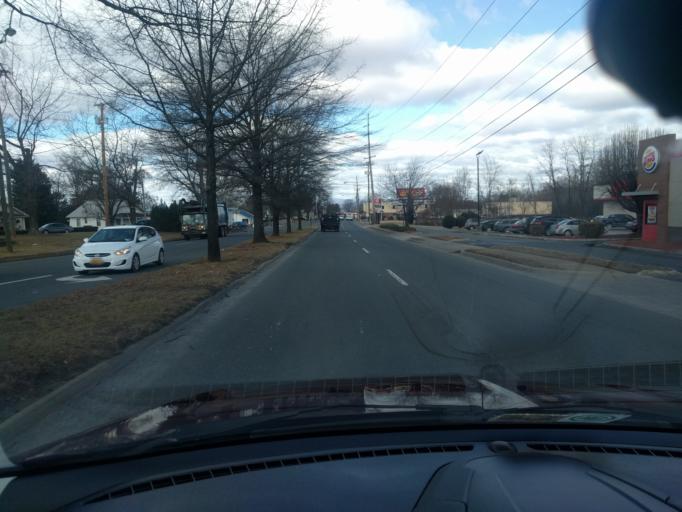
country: US
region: Virginia
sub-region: City of Lynchburg
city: Lynchburg
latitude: 37.3806
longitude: -79.1340
